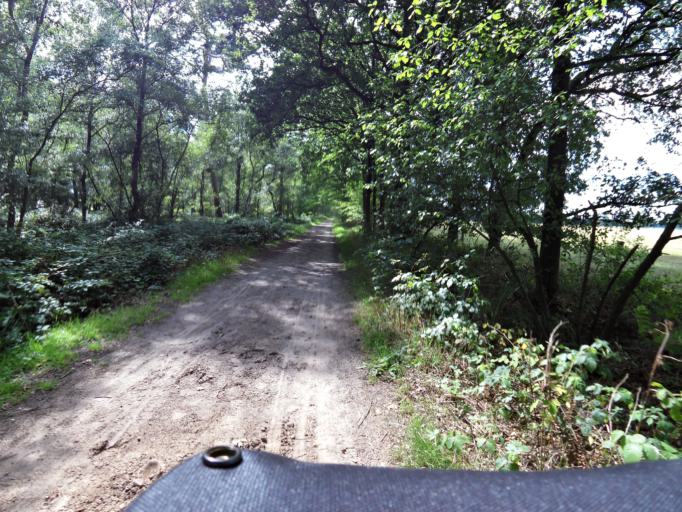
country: BE
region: Flanders
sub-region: Provincie Antwerpen
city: Hoogstraten
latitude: 51.4130
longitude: 4.8200
